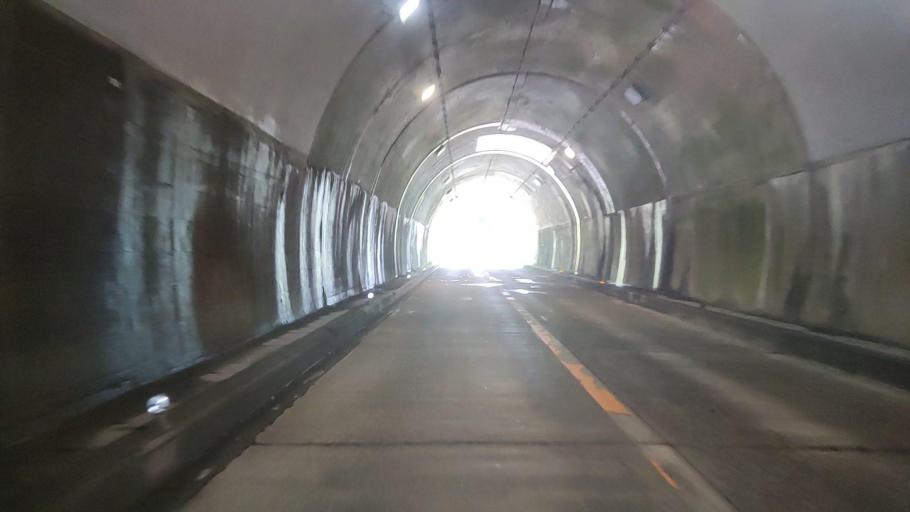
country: JP
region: Wakayama
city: Shingu
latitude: 33.8174
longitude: 135.8561
